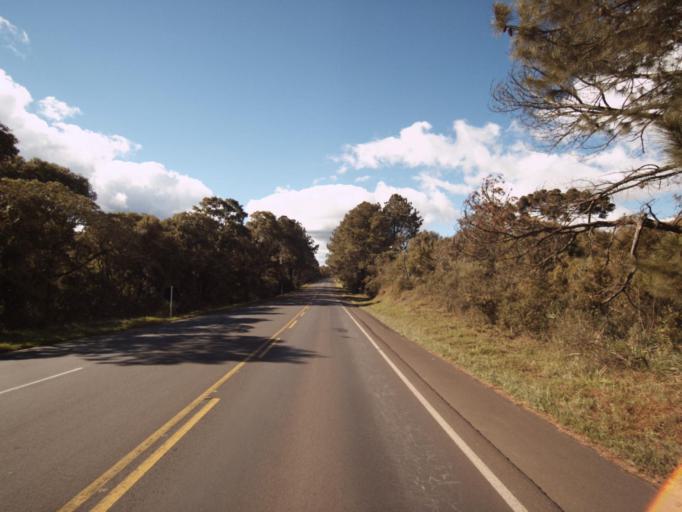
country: BR
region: Santa Catarina
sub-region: Joacaba
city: Joacaba
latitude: -26.9781
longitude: -51.7830
